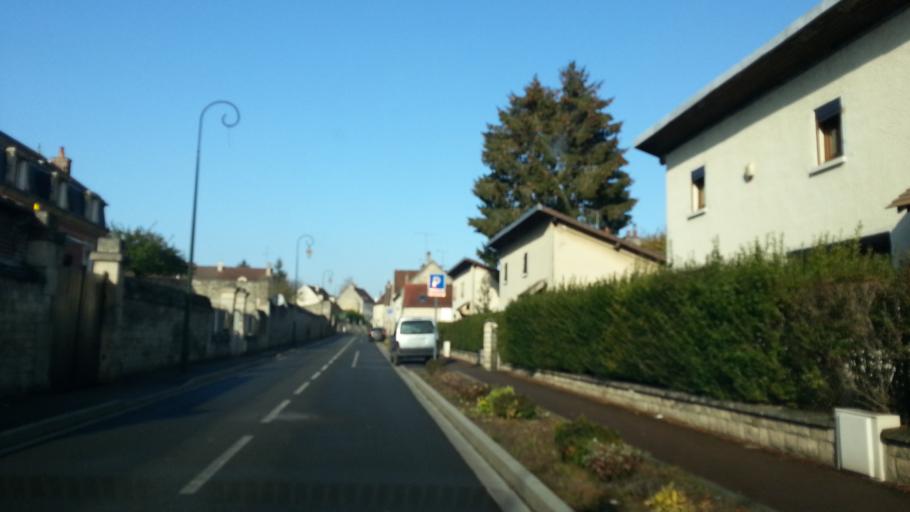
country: FR
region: Picardie
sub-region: Departement de l'Oise
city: Balagny-sur-Therain
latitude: 49.2927
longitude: 2.3383
